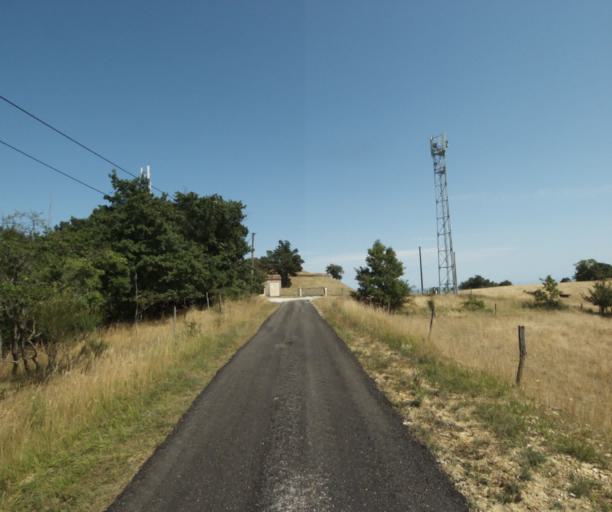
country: FR
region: Midi-Pyrenees
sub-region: Departement de la Haute-Garonne
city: Saint-Felix-Lauragais
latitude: 43.4408
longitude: 1.8827
